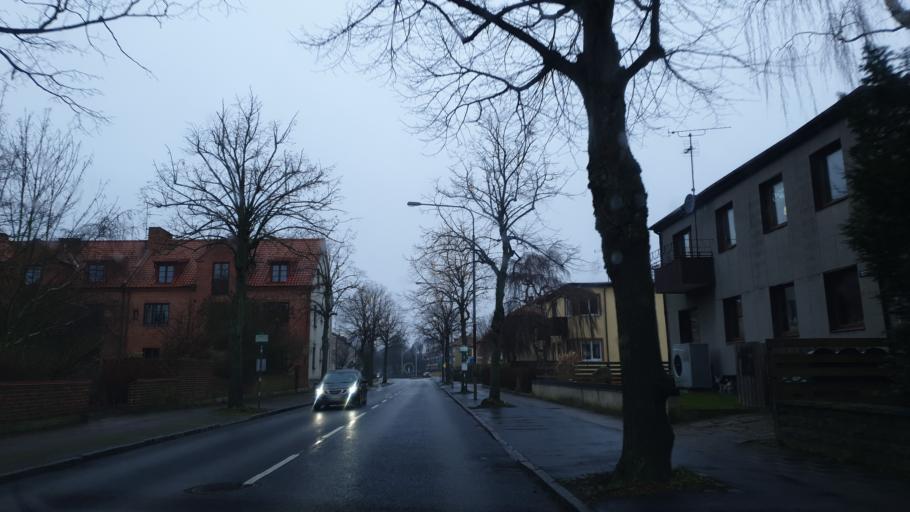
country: SE
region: Skane
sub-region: Trelleborgs Kommun
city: Trelleborg
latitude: 55.3781
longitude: 13.1699
